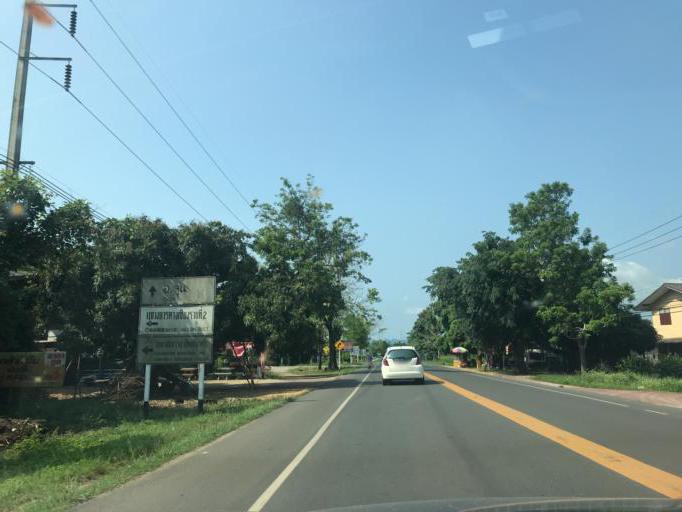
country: TH
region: Phayao
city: Chiang Kham
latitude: 19.4953
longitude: 100.2775
